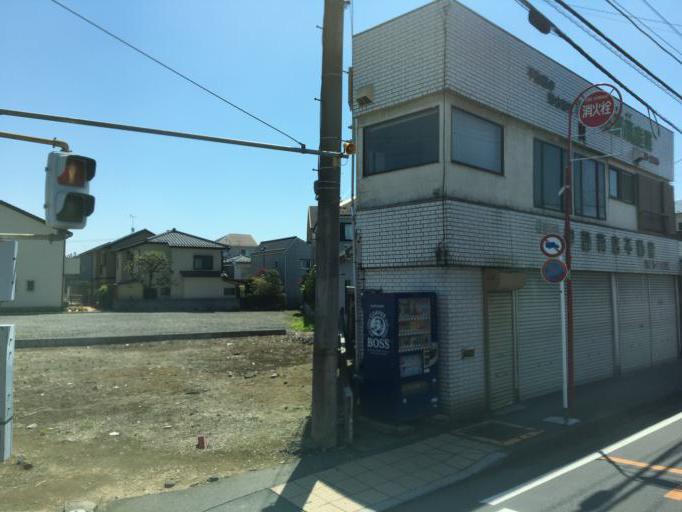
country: JP
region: Saitama
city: Kawagoe
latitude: 35.9313
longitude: 139.4805
